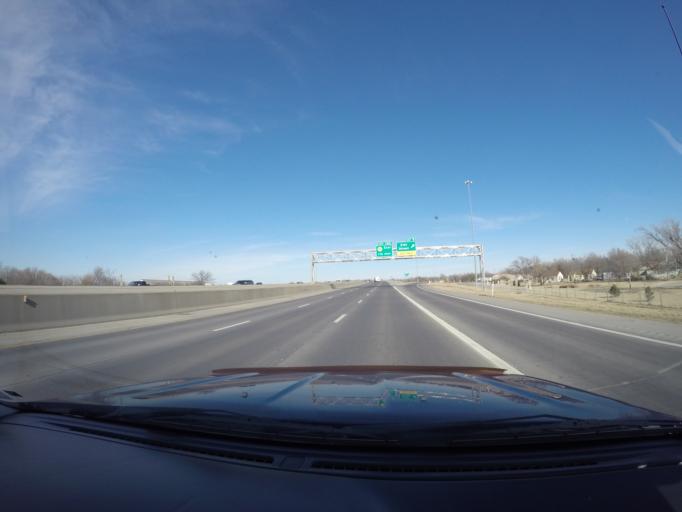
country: US
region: Kansas
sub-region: Sedgwick County
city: Wichita
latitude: 37.7192
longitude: -97.3202
